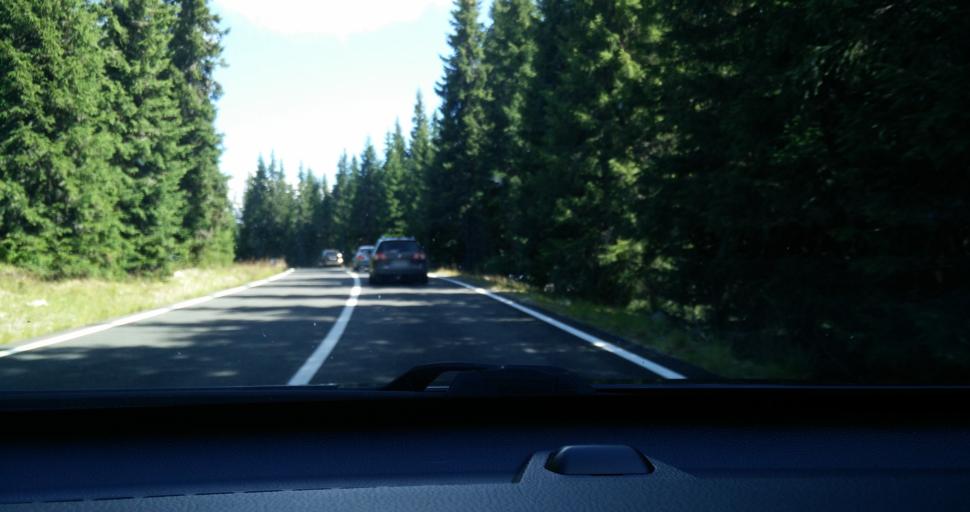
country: RO
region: Hunedoara
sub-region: Oras Petrila
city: Petrila
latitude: 45.4693
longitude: 23.6333
